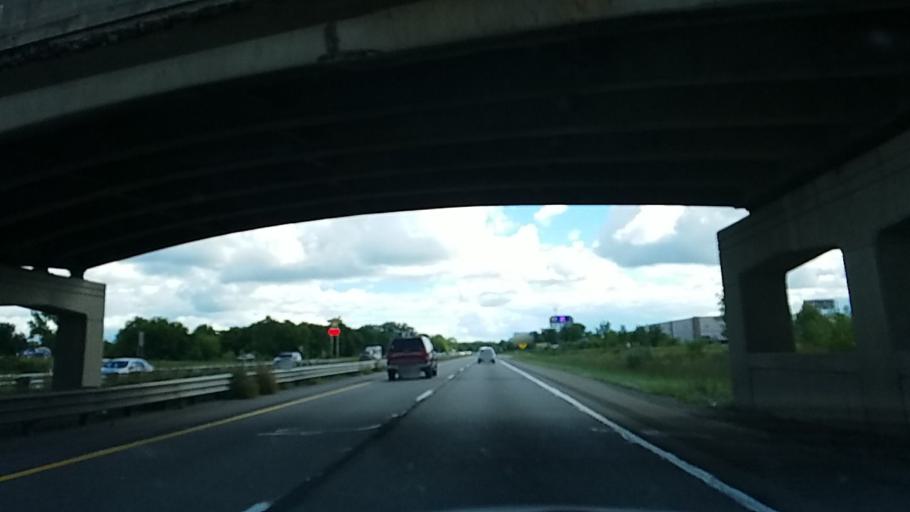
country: US
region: Michigan
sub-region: Livingston County
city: Whitmore Lake
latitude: 42.3796
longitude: -83.7572
